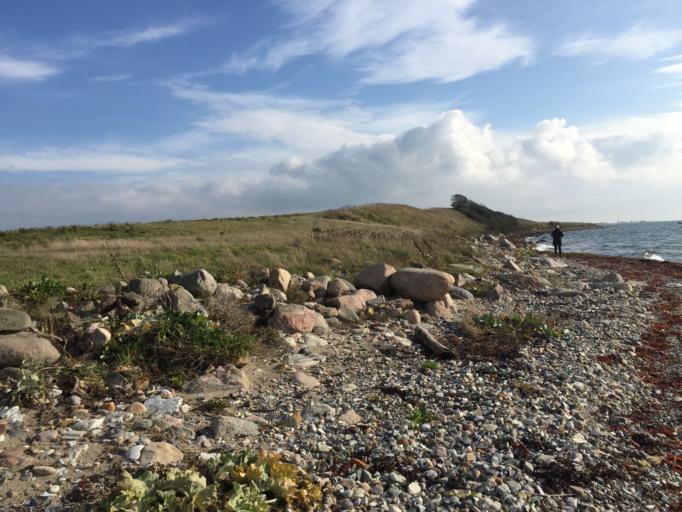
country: DK
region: Zealand
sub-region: Slagelse Kommune
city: Skaelskor
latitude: 55.1977
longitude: 11.1768
